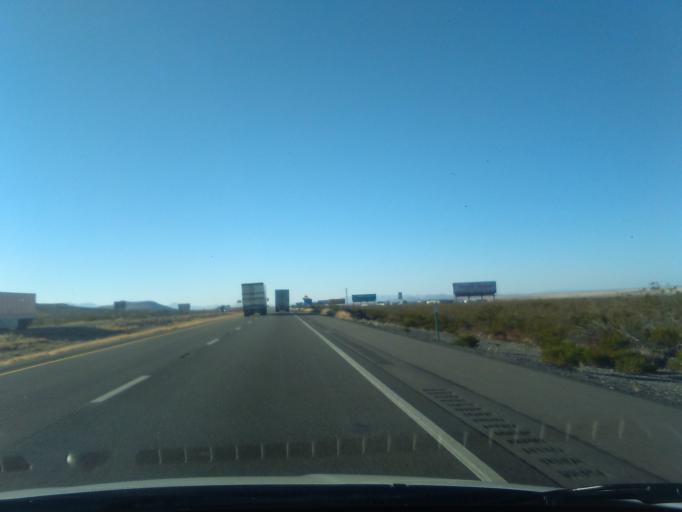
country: US
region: New Mexico
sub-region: Hidalgo County
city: Lordsburg
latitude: 32.3472
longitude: -108.7253
